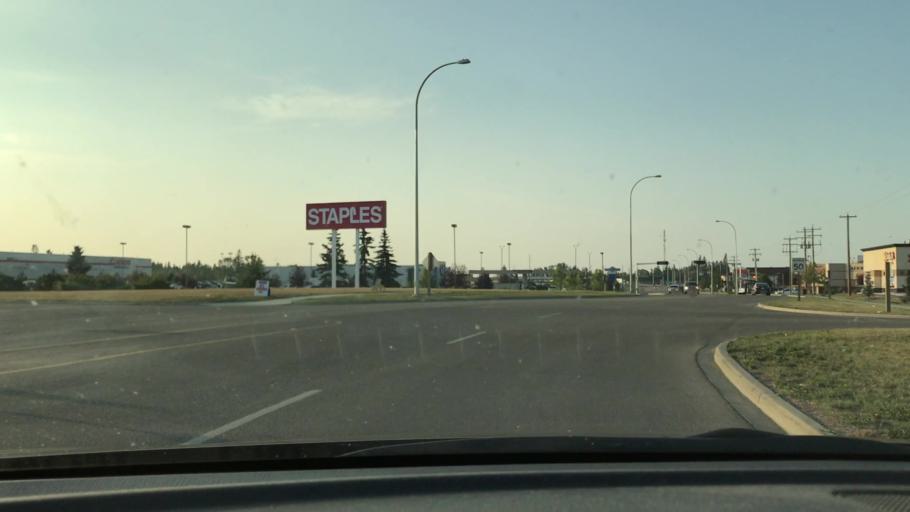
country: CA
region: Alberta
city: Red Deer
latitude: 52.2112
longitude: -113.8162
